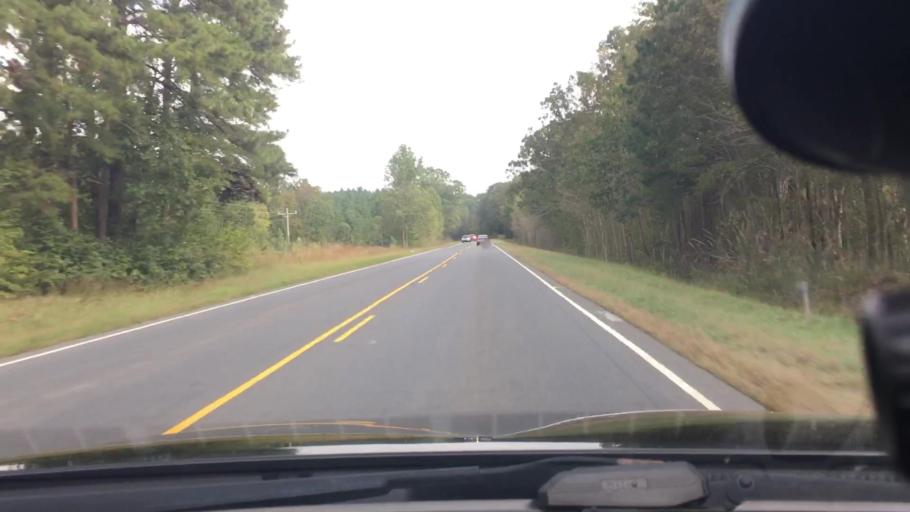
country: US
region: North Carolina
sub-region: Montgomery County
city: Mount Gilead
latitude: 35.3056
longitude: -80.0355
